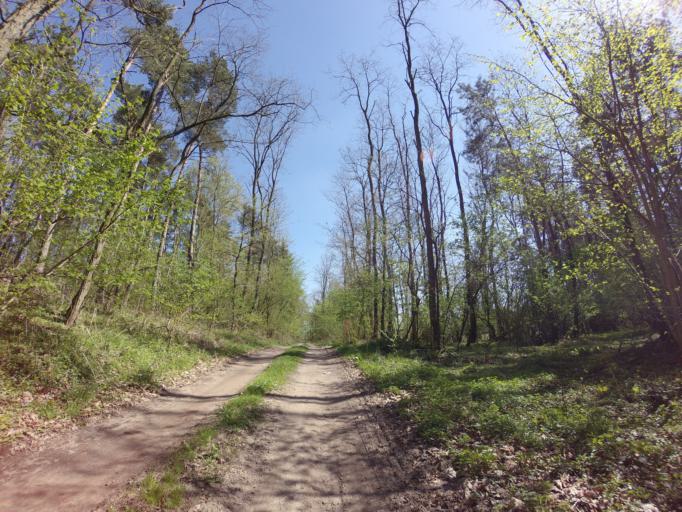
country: PL
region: West Pomeranian Voivodeship
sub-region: Powiat choszczenski
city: Choszczno
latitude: 53.1816
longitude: 15.3611
